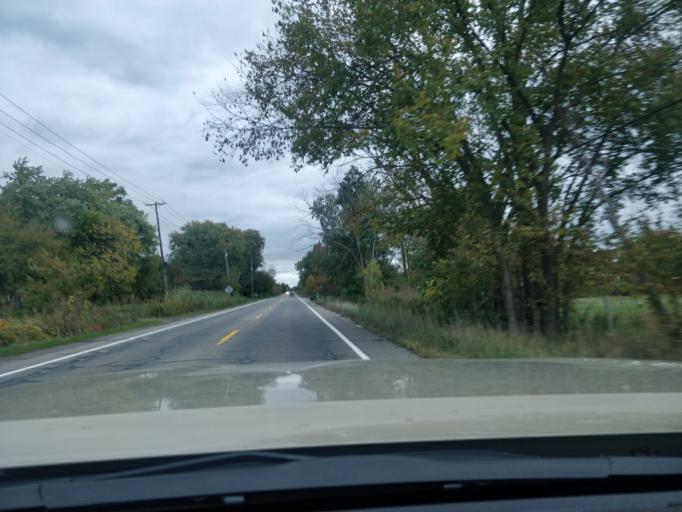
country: US
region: Michigan
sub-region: Wayne County
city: Romulus
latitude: 42.1809
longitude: -83.3330
